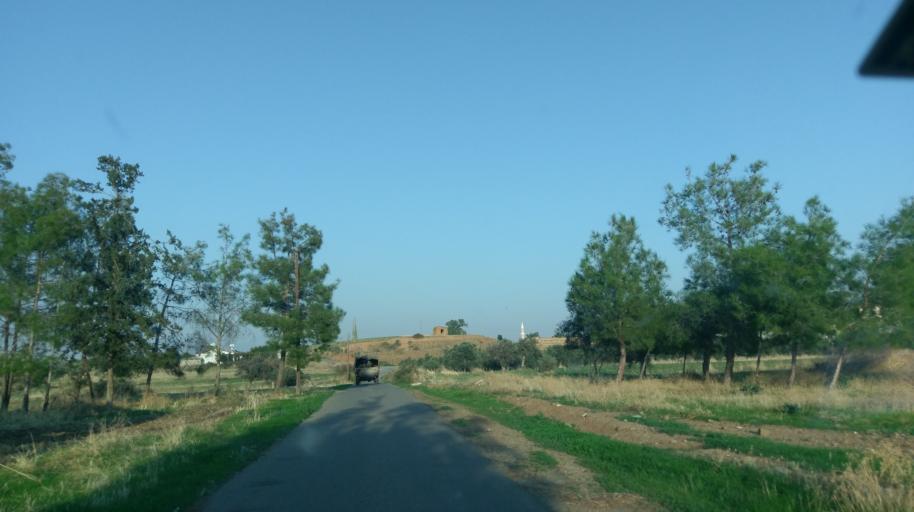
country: CY
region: Lefkosia
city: Lefka
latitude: 35.1164
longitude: 32.9433
